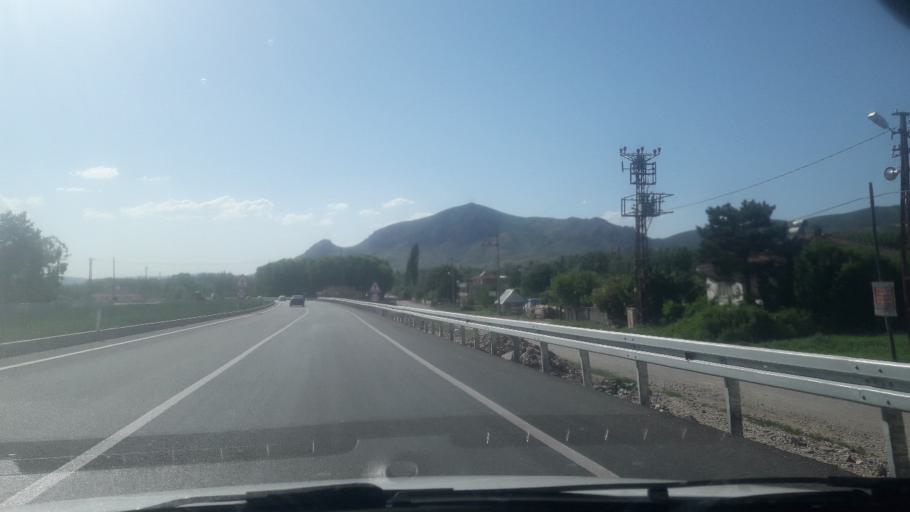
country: TR
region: Tokat
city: Dokmetepe
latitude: 40.3208
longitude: 36.2318
